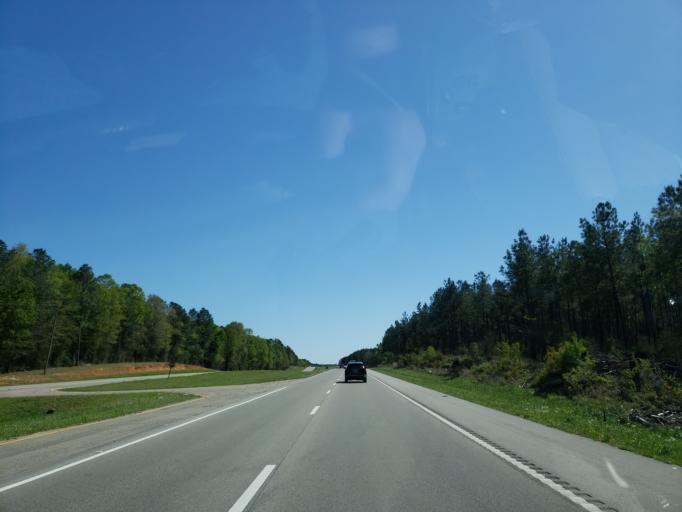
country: US
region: Mississippi
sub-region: Stone County
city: Wiggins
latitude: 31.0124
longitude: -89.2022
